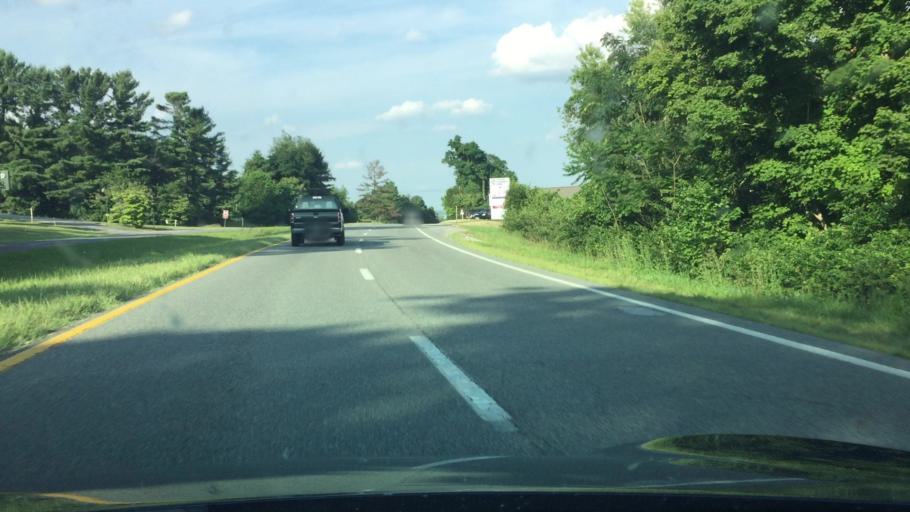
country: US
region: Virginia
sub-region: Pulaski County
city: Fairlawn
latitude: 37.1458
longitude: -80.6017
